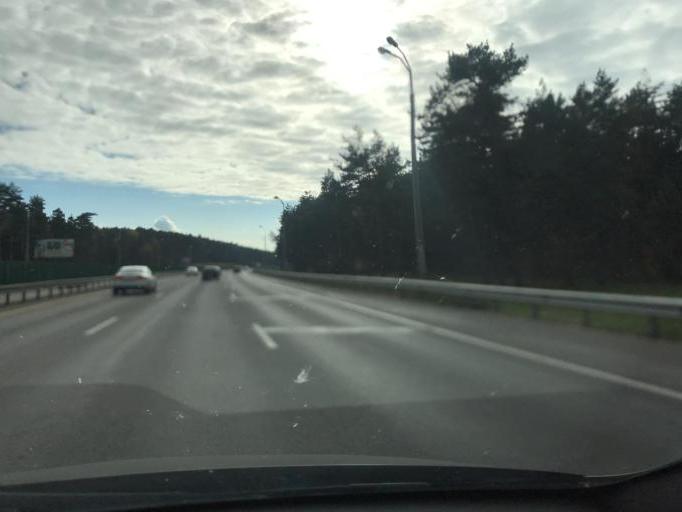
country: BY
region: Minsk
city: Vyaliki Trastsyanets
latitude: 53.8818
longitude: 27.6967
